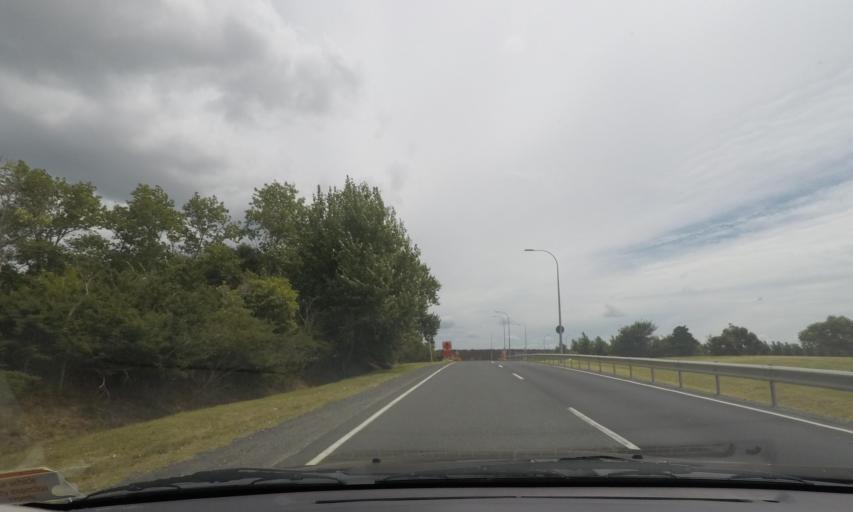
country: NZ
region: Auckland
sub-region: Auckland
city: Mangere
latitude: -36.9929
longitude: 174.7880
